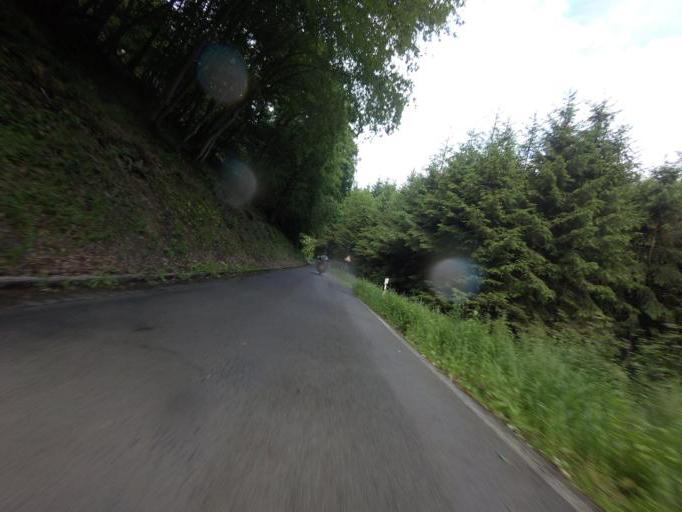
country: DE
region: Rheinland-Pfalz
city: Kottenborn
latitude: 50.3598
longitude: 6.8893
